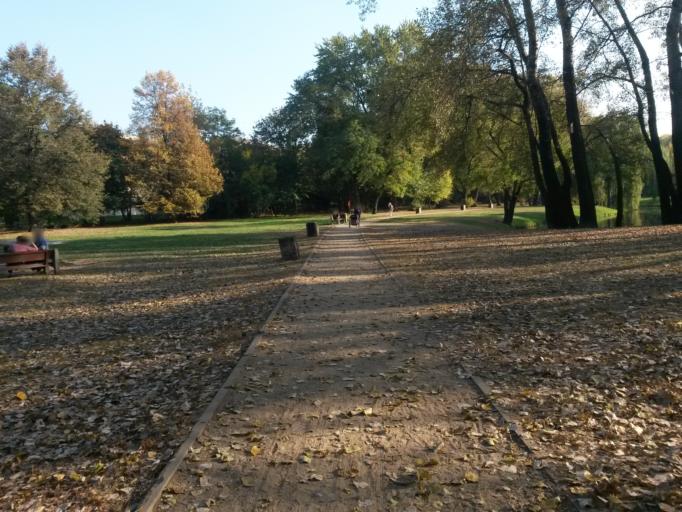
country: PL
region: Masovian Voivodeship
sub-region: Warszawa
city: Mokotow
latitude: 52.2013
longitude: 21.0399
